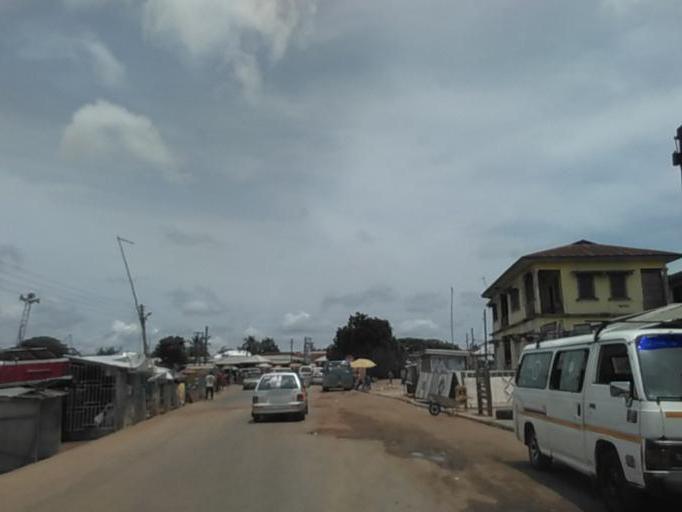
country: GH
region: Ashanti
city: Mamponteng
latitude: 6.8357
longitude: -1.5151
